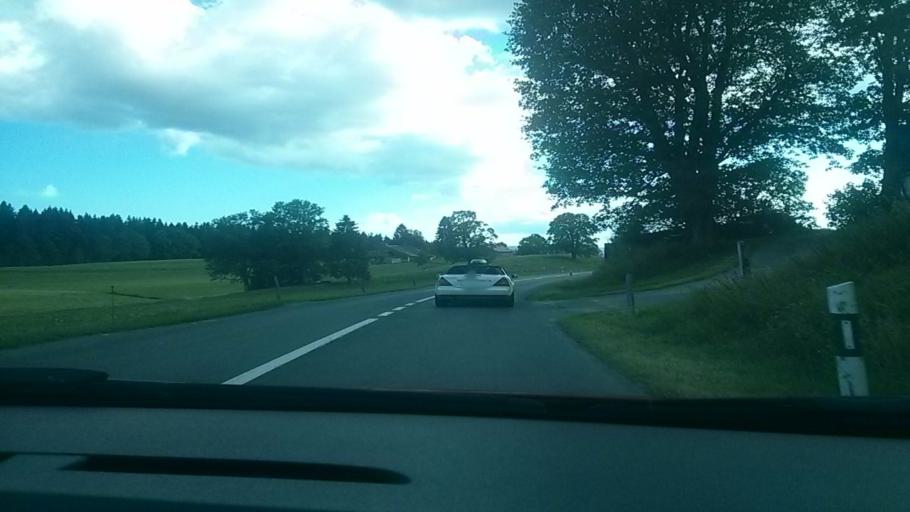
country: CH
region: Vaud
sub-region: Jura-Nord vaudois District
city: Le Chenit
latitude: 46.6266
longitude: 6.2443
